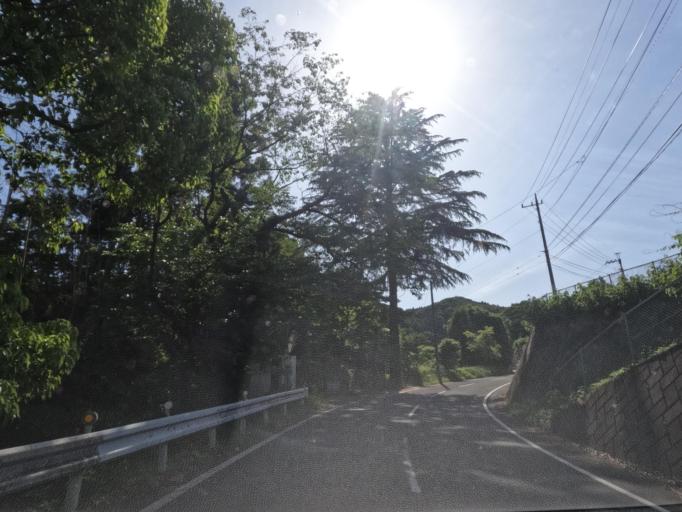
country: JP
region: Saitama
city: Yorii
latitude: 36.0470
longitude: 139.1684
